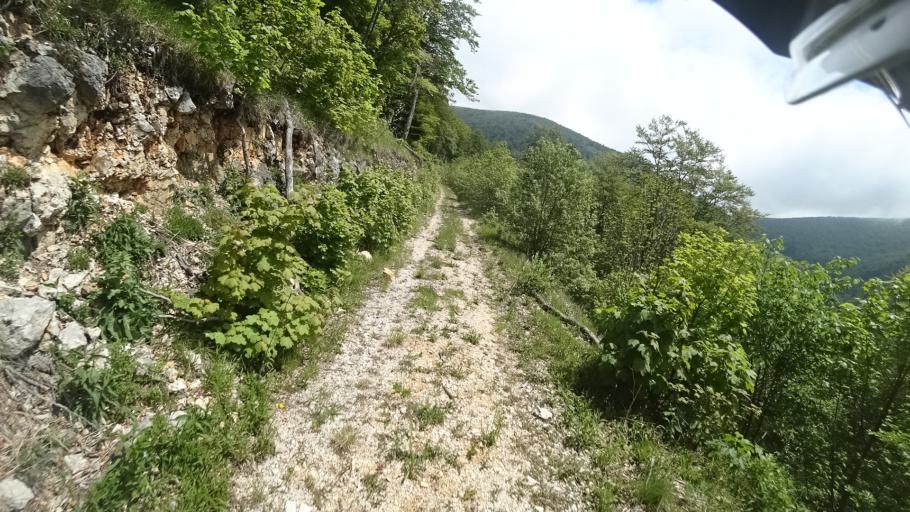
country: BA
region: Federation of Bosnia and Herzegovina
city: Orasac
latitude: 44.5676
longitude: 15.8622
